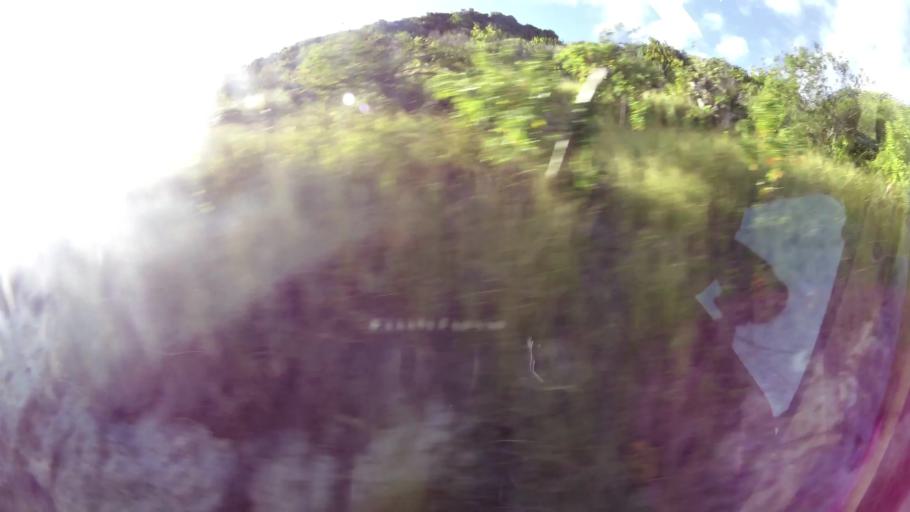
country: MS
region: Saint Peter
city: Brades
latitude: 16.8077
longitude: -62.1925
